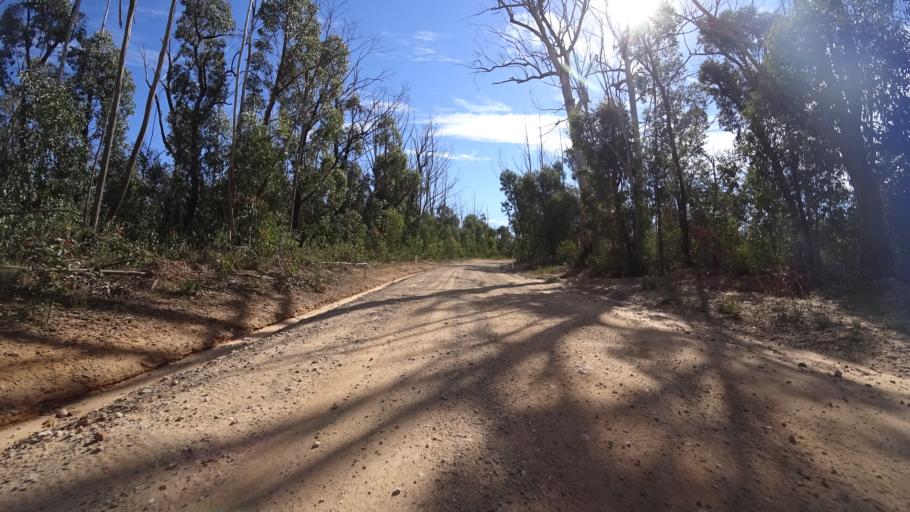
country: AU
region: New South Wales
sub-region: Lithgow
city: Lithgow
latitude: -33.4352
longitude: 150.1848
